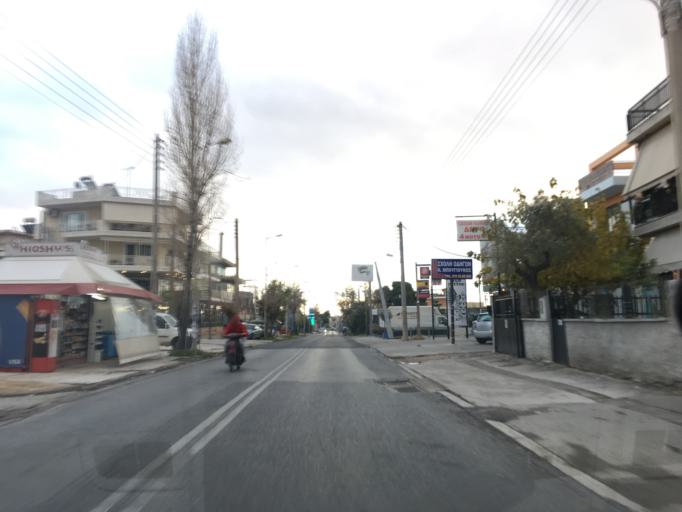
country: GR
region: Attica
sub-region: Nomarchia Athinas
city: Nea Filadelfeia
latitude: 38.0514
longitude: 23.7298
